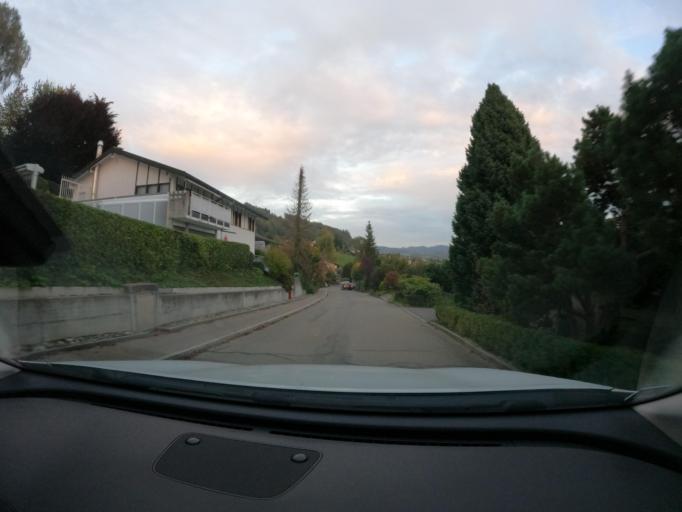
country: CH
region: Bern
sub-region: Bern-Mittelland District
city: Stettlen
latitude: 46.9599
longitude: 7.5319
